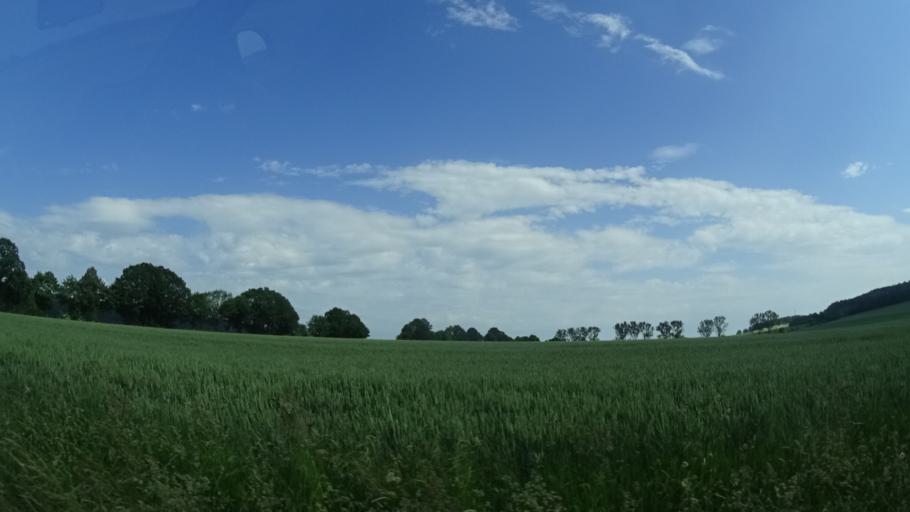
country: DE
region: Hesse
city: Haina
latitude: 51.0157
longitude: 8.9600
